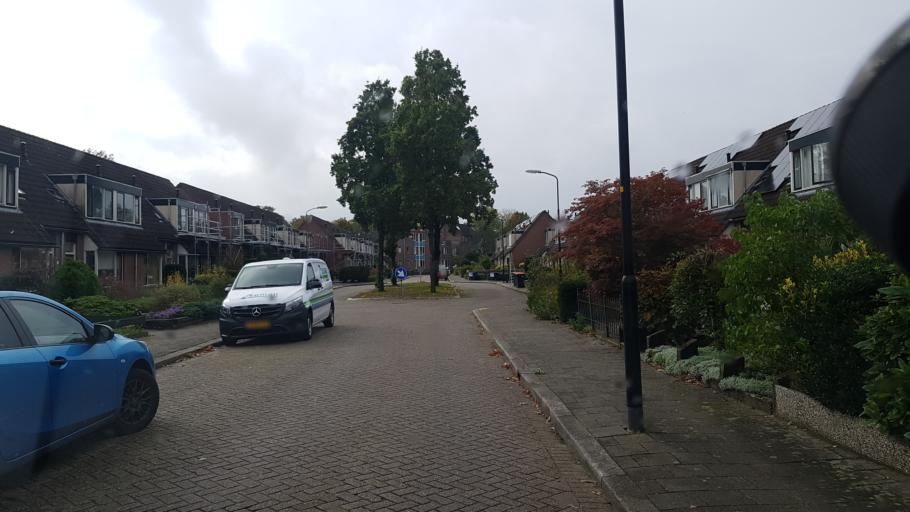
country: NL
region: Gelderland
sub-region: Gemeente Apeldoorn
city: Apeldoorn
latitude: 52.2018
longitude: 5.9617
